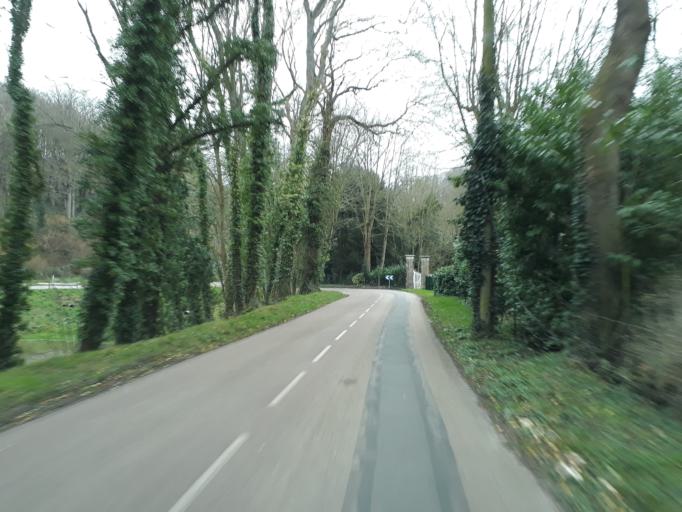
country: FR
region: Haute-Normandie
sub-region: Departement de la Seine-Maritime
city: Yport
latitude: 49.7327
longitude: 0.2912
